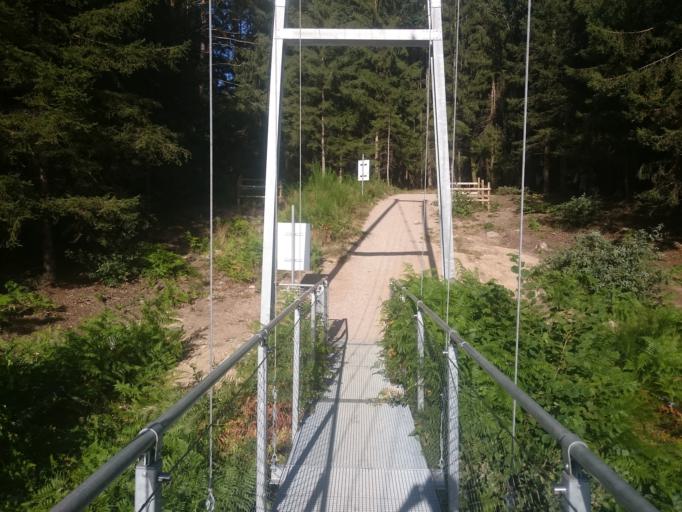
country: FR
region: Auvergne
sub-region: Departement du Cantal
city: Laroquebrou
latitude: 44.9363
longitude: 2.2259
